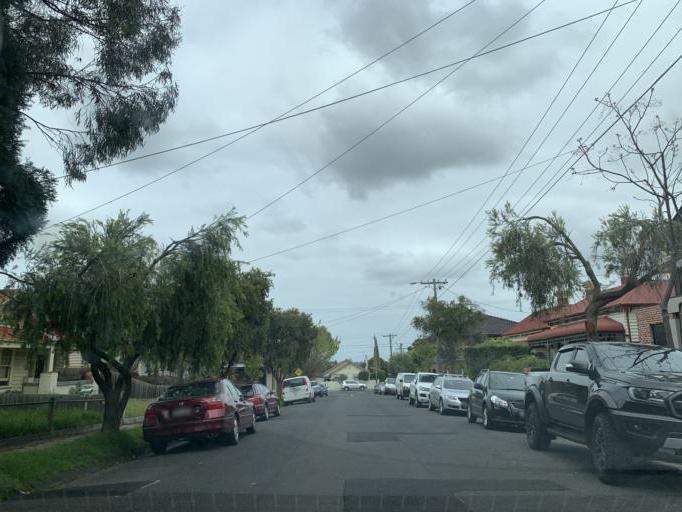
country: AU
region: Victoria
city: Brunswick West
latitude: -37.7530
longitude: 144.9506
